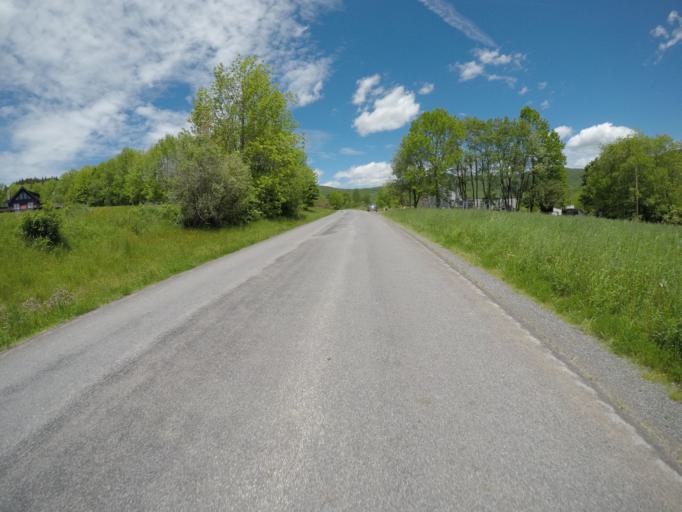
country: US
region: New York
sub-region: Delaware County
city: Stamford
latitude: 42.2677
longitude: -74.5189
